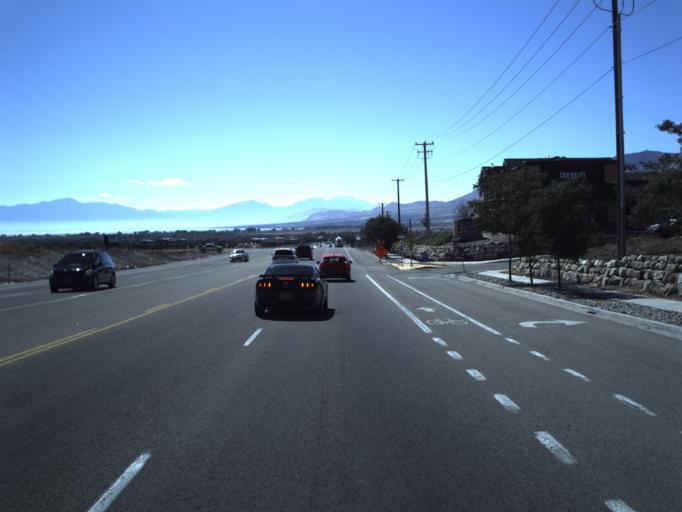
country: US
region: Utah
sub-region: Utah County
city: Saratoga Springs
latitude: 40.3987
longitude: -111.9191
